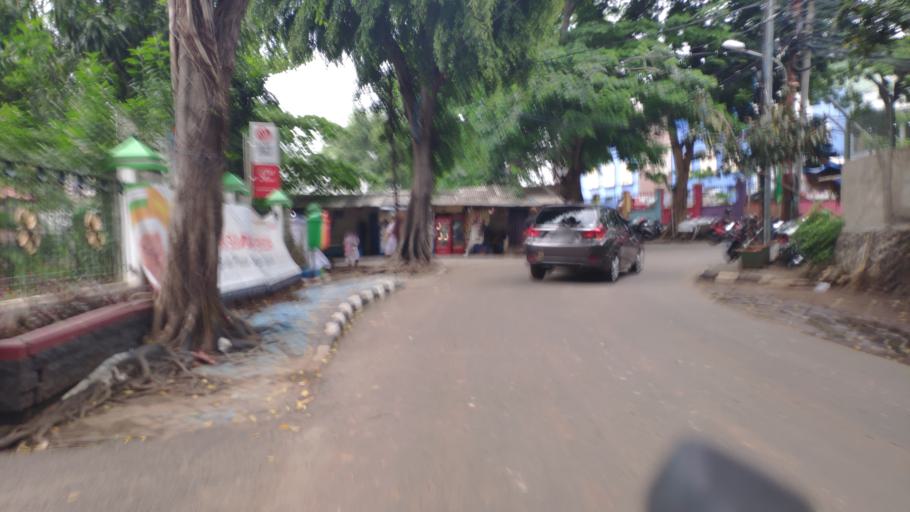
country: ID
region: Jakarta Raya
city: Jakarta
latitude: -6.2218
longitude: 106.8385
